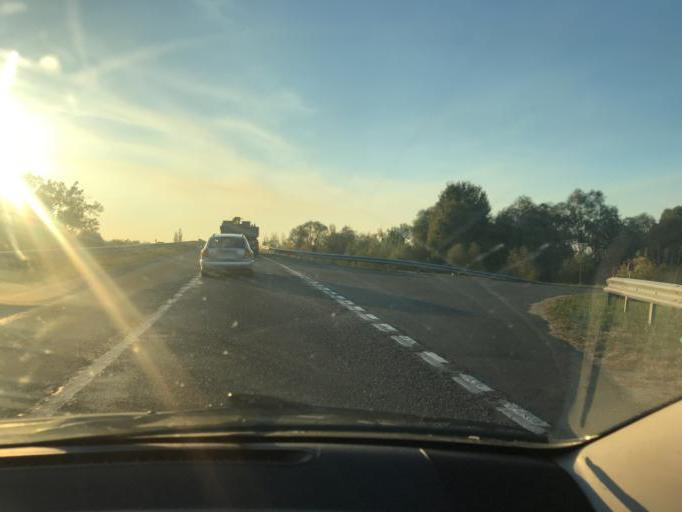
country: BY
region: Brest
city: Pinsk
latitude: 52.0737
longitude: 26.1630
